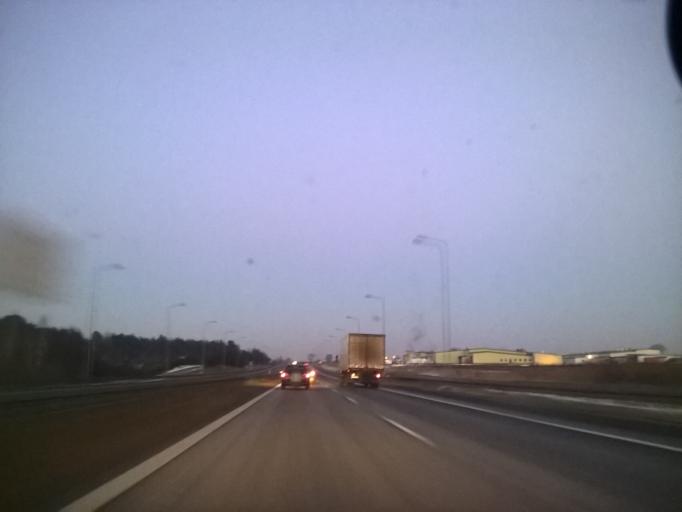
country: PL
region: Warmian-Masurian Voivodeship
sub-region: Powiat olsztynski
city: Biskupiec
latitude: 53.8470
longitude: 20.9515
